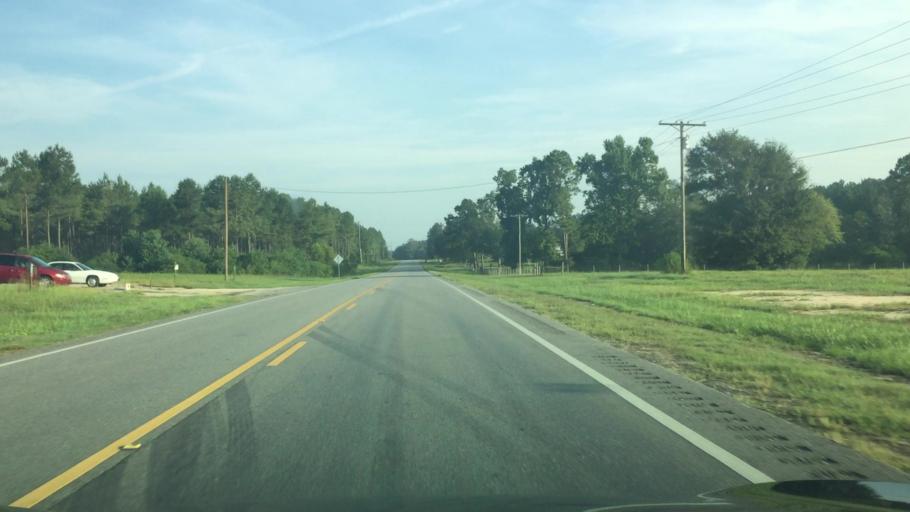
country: US
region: Alabama
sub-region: Covington County
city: Florala
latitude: 31.0169
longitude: -86.3613
